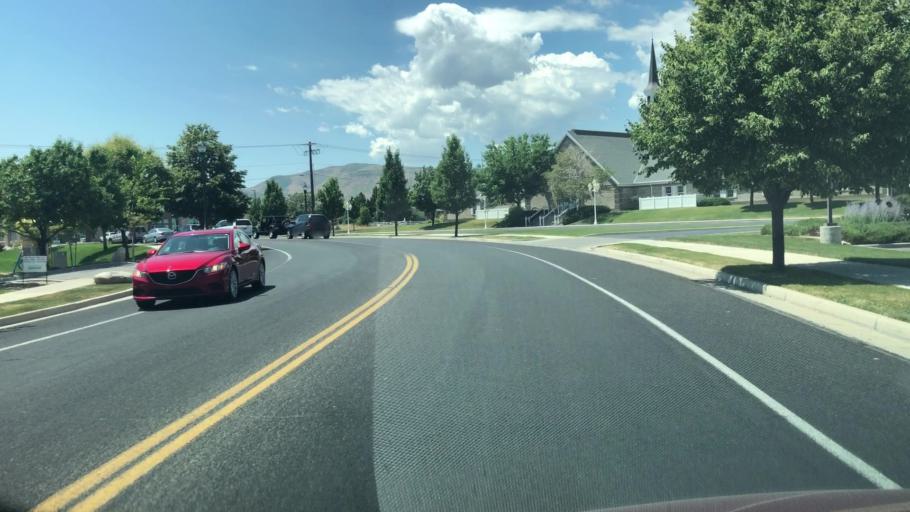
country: US
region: Utah
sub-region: Salt Lake County
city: Herriman
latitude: 40.5233
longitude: -111.9869
